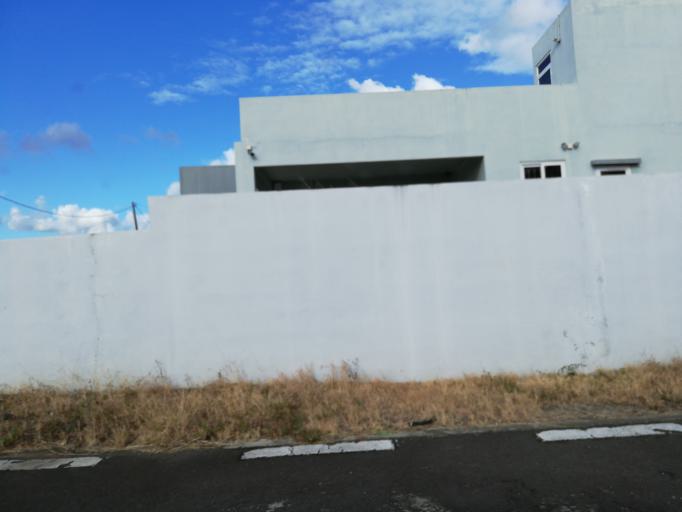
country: MU
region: Black River
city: Petite Riviere
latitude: -20.2015
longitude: 57.4613
